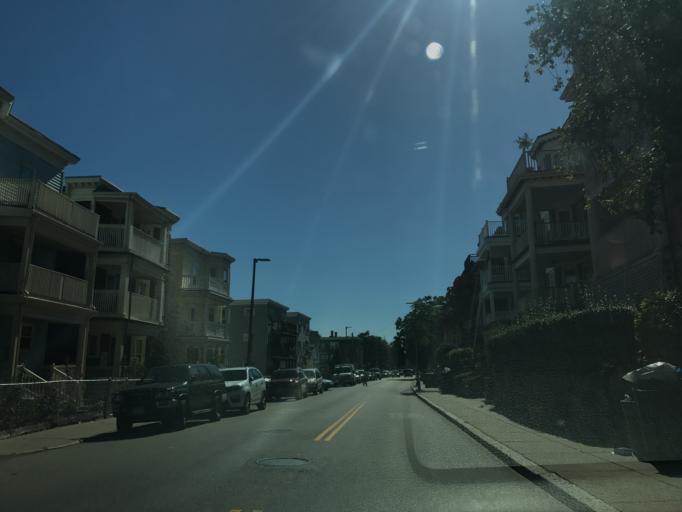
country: US
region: Massachusetts
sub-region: Suffolk County
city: South Boston
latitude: 42.3066
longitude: -71.0622
